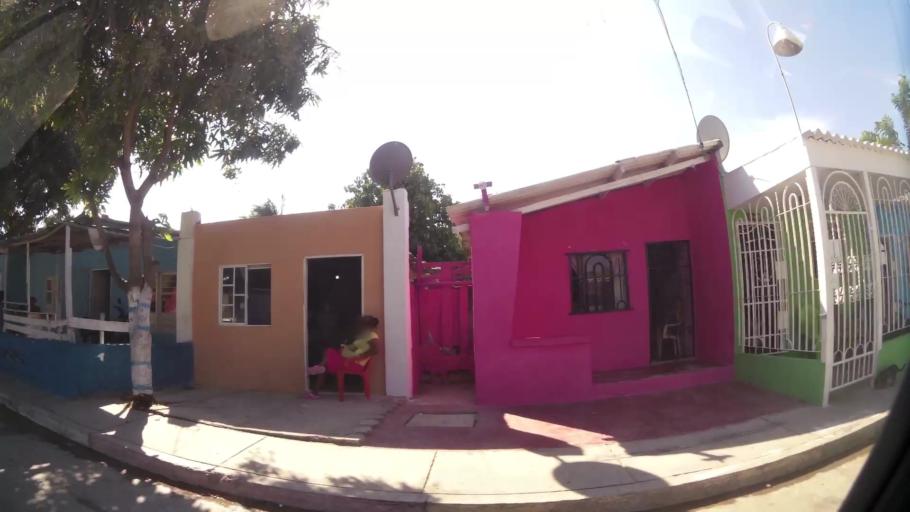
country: CO
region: Atlantico
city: Barranquilla
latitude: 10.9300
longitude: -74.8183
